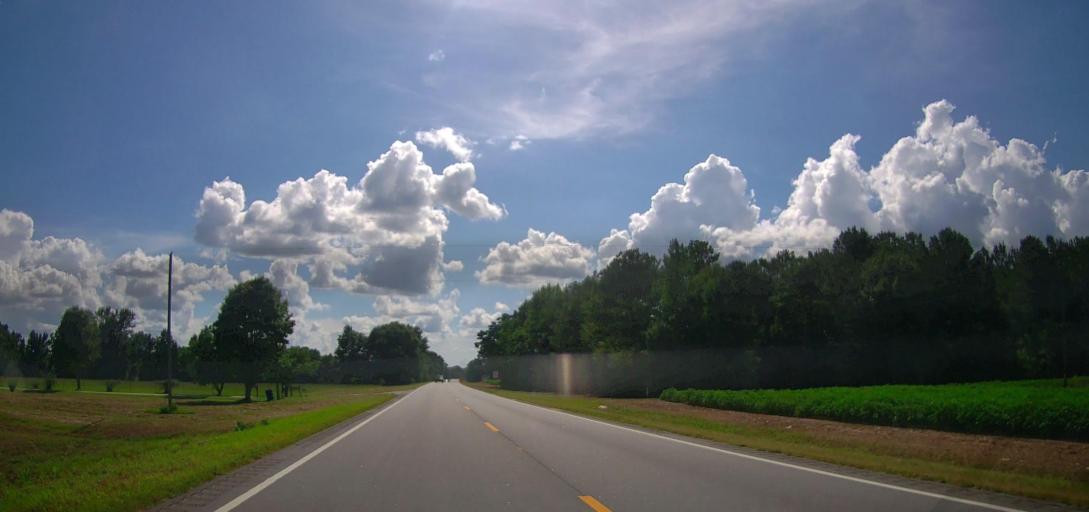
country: US
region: Alabama
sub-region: Lee County
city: Auburn
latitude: 32.4310
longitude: -85.4288
